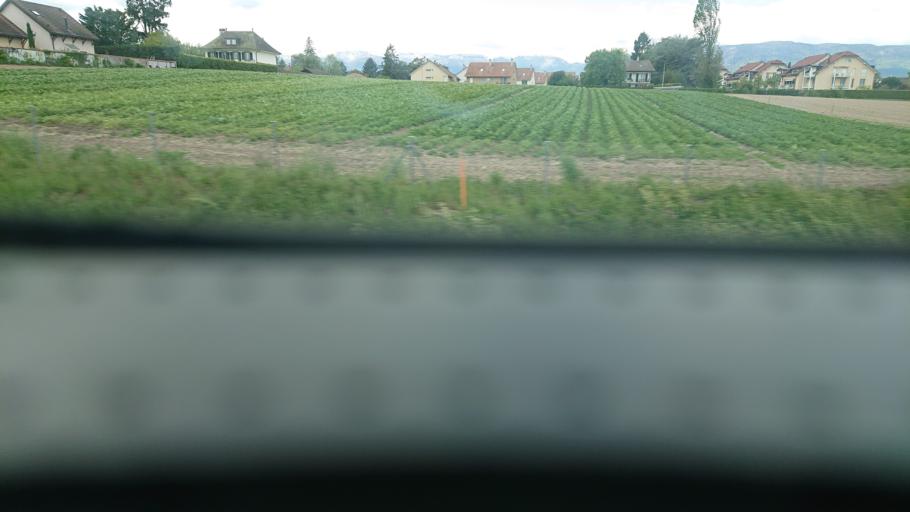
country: CH
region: Vaud
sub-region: Nyon District
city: Coppet
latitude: 46.3145
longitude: 6.1868
